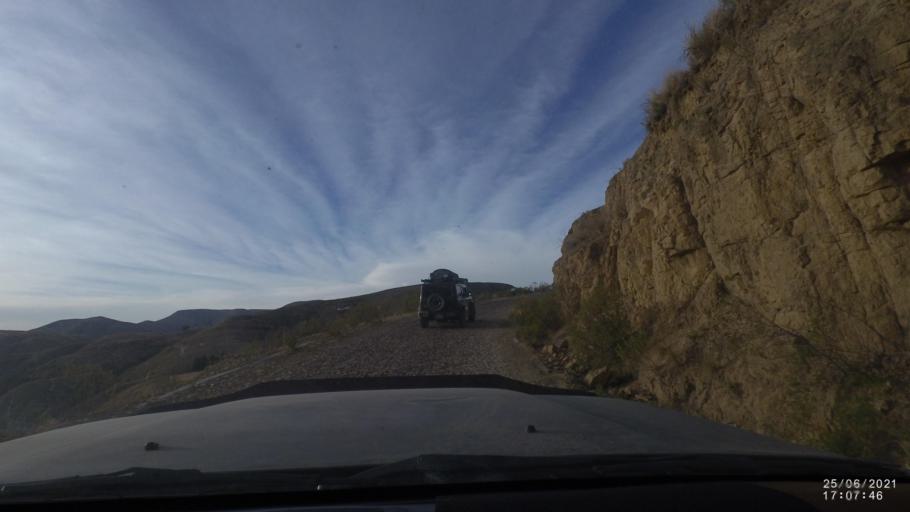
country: BO
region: Cochabamba
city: Arani
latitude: -17.8381
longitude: -65.7108
